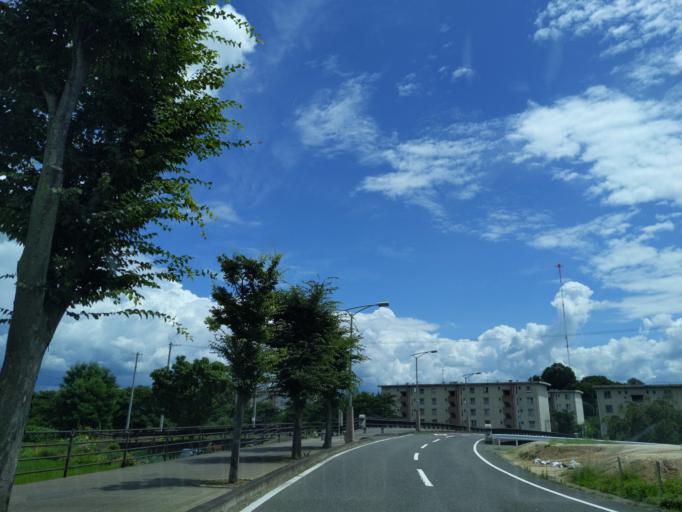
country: JP
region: Fukushima
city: Koriyama
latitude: 37.3642
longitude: 140.3529
